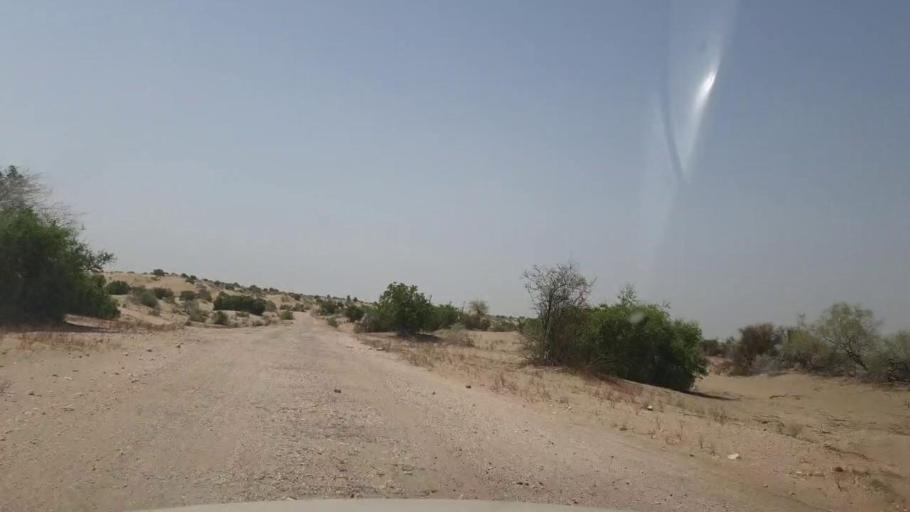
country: PK
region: Sindh
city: Khanpur
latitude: 27.4132
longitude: 69.3194
